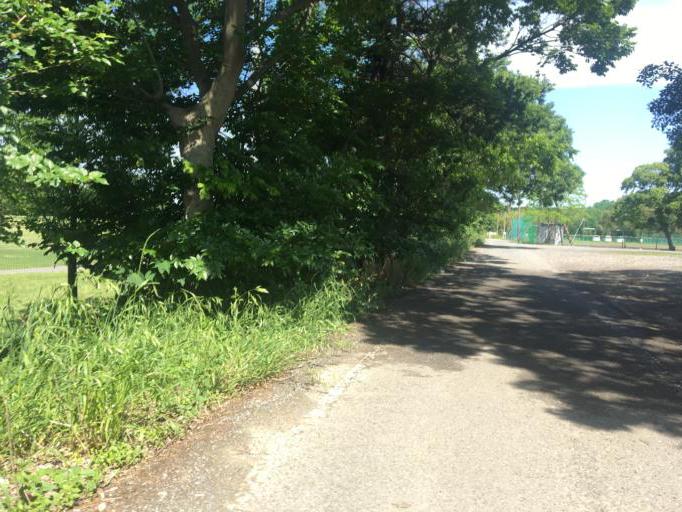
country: JP
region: Saitama
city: Shiki
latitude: 35.8596
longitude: 139.5895
